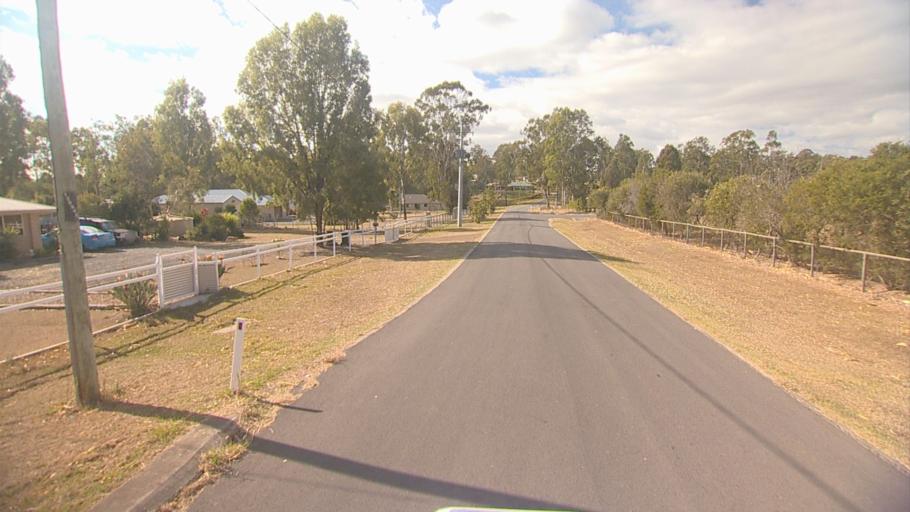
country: AU
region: Queensland
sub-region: Logan
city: Cedar Vale
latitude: -27.8741
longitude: 152.9985
